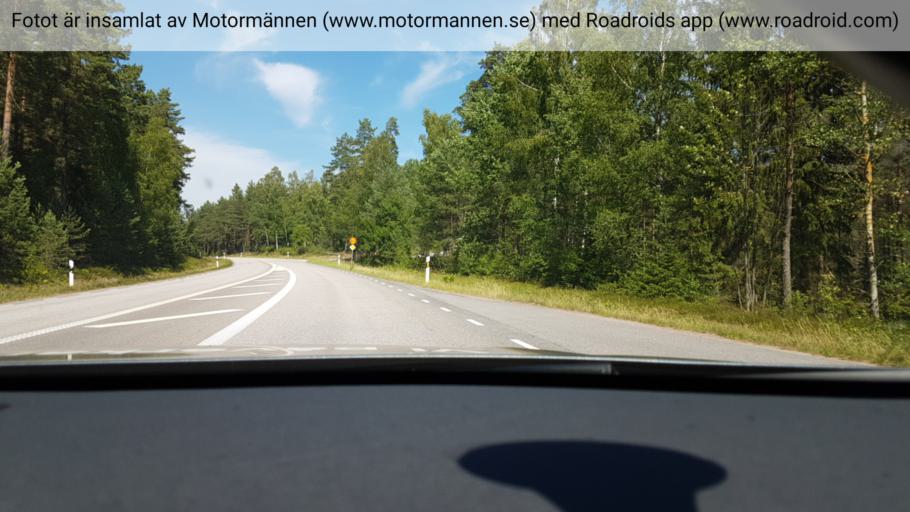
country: SE
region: Vaestra Goetaland
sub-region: Skovde Kommun
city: Stopen
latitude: 58.4531
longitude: 13.9541
